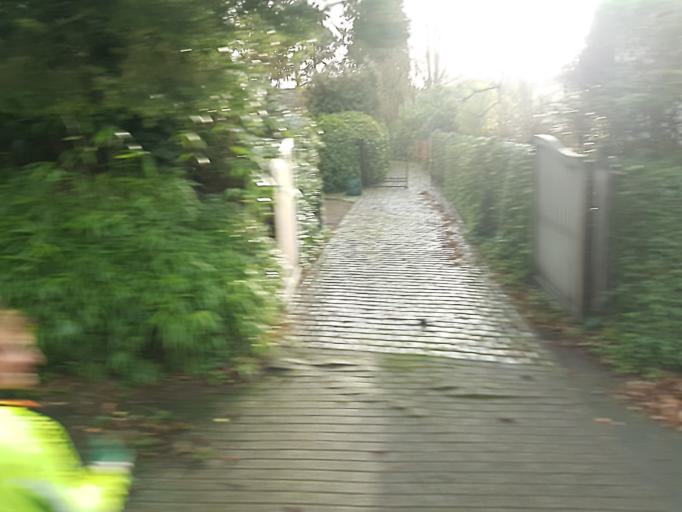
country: BE
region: Flanders
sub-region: Provincie Antwerpen
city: Kapellen
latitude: 51.3107
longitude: 4.4484
